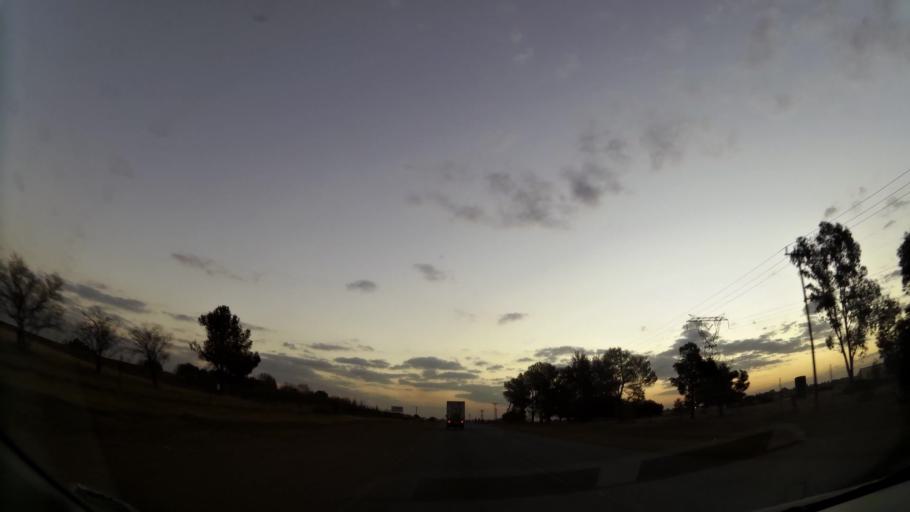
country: ZA
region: Gauteng
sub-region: West Rand District Municipality
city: Krugersdorp
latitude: -26.0712
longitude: 27.6680
